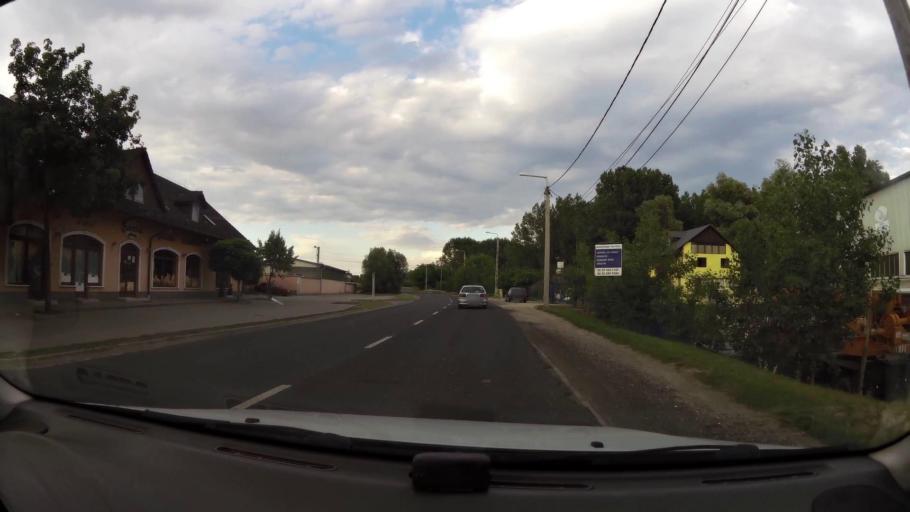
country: HU
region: Pest
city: Suelysap
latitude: 47.4453
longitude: 19.5510
